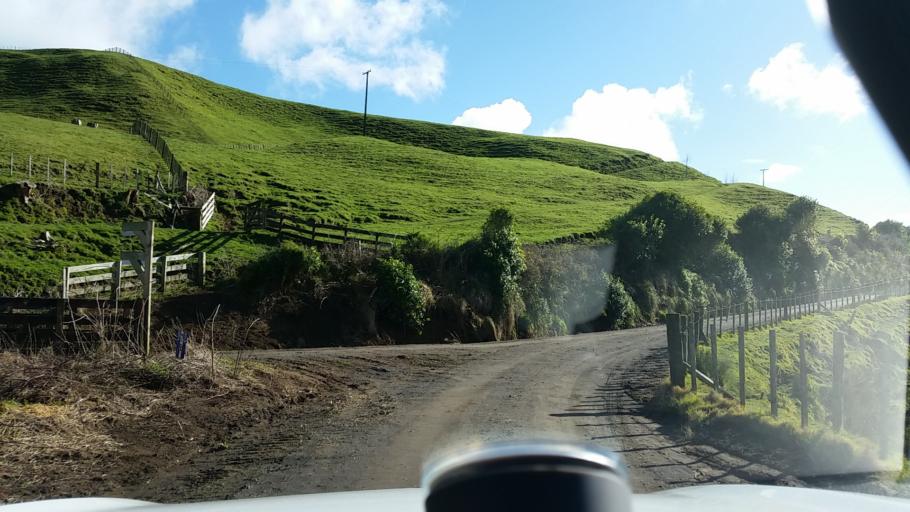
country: NZ
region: Taranaki
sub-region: South Taranaki District
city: Eltham
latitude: -39.4574
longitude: 174.3694
